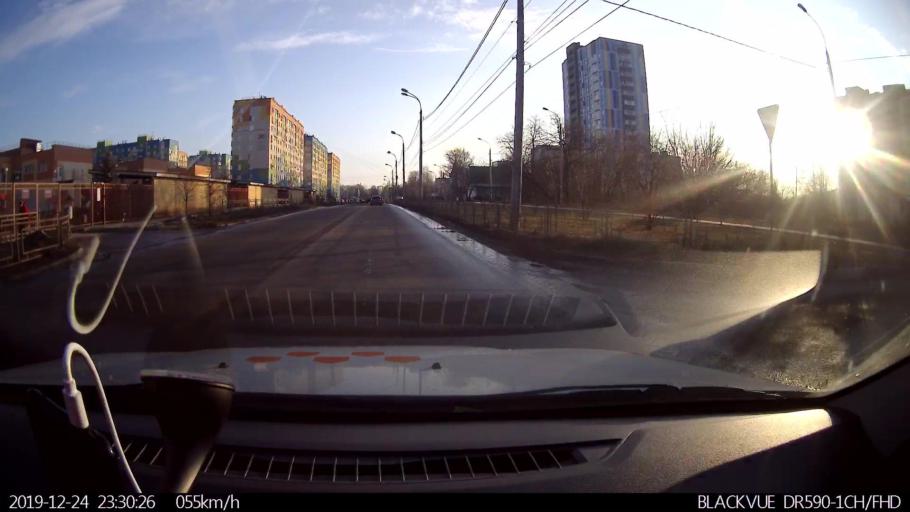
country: RU
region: Nizjnij Novgorod
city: Gorbatovka
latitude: 56.2355
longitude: 43.8418
